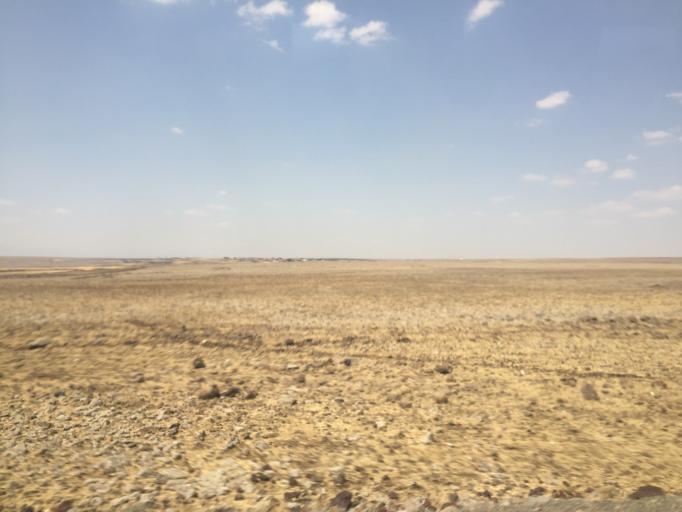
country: TR
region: Sanliurfa
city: Siverek
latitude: 37.7769
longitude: 39.4599
